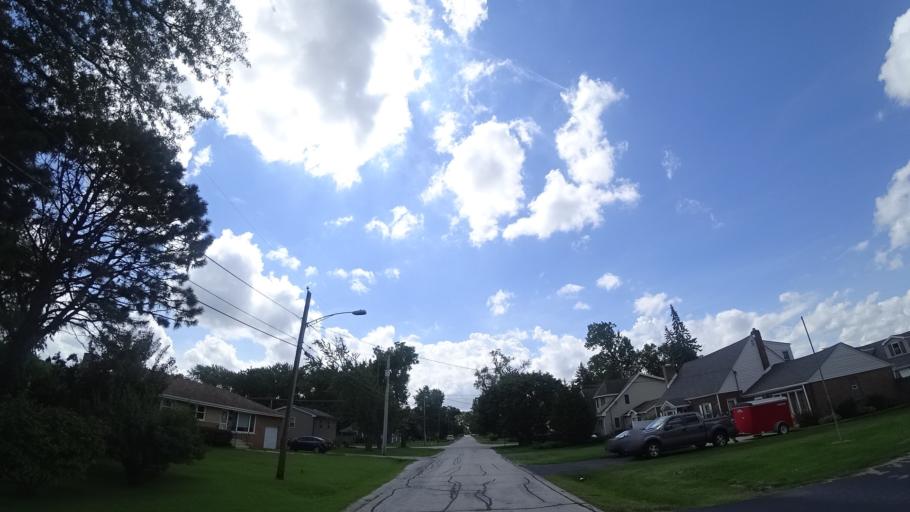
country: US
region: Illinois
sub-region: Cook County
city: Tinley Park
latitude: 41.5702
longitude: -87.7830
